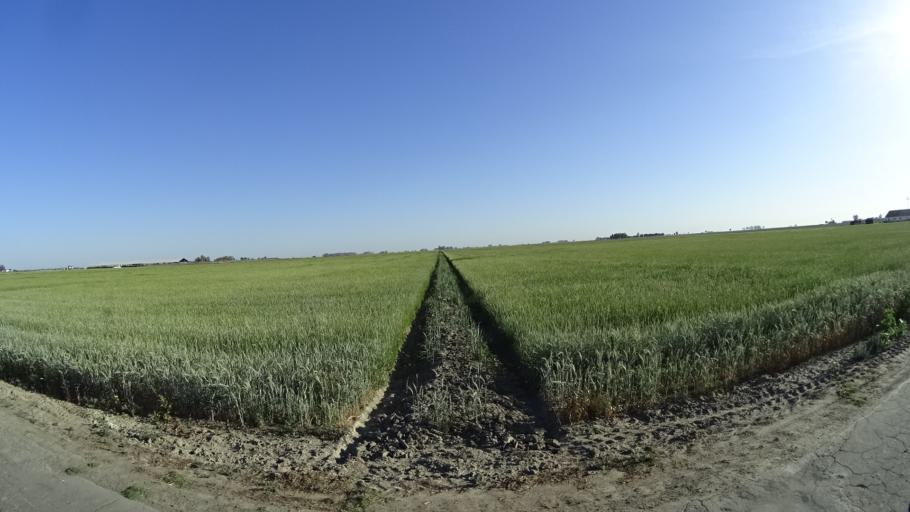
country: US
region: California
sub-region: Kings County
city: Stratford
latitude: 36.1600
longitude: -119.7913
